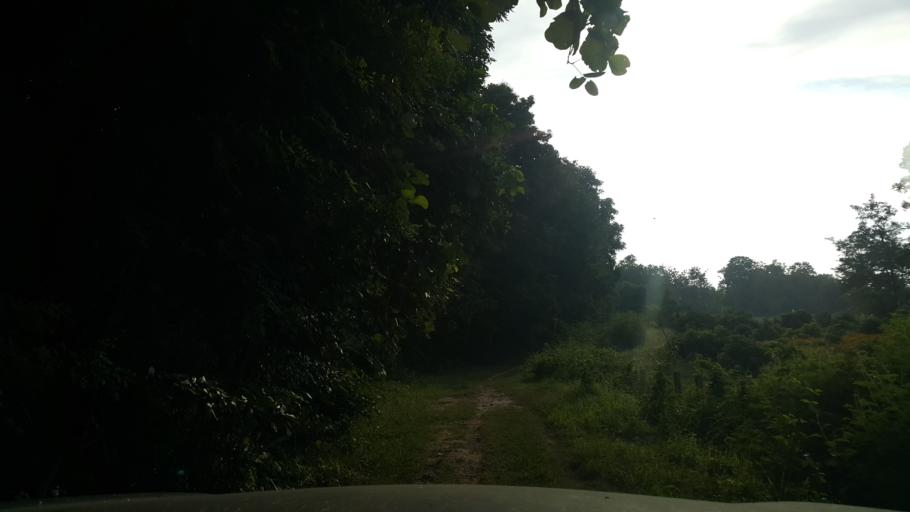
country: TH
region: Chiang Mai
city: San Sai
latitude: 18.9257
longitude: 99.0496
